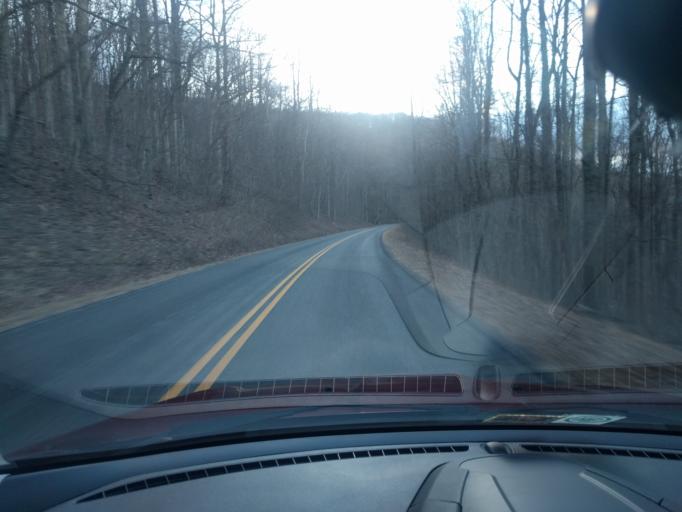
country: US
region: Virginia
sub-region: Botetourt County
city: Buchanan
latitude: 37.4549
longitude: -79.6247
